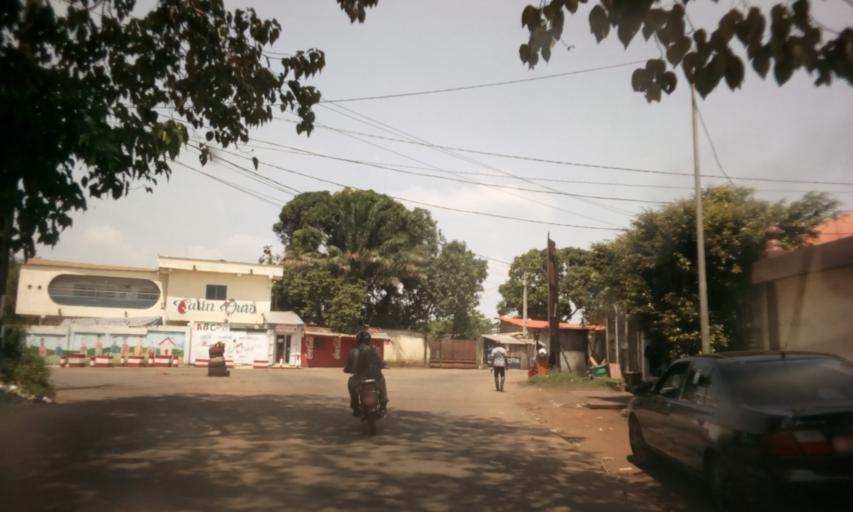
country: GN
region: Conakry
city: Conakry
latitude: 9.5771
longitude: -13.6641
